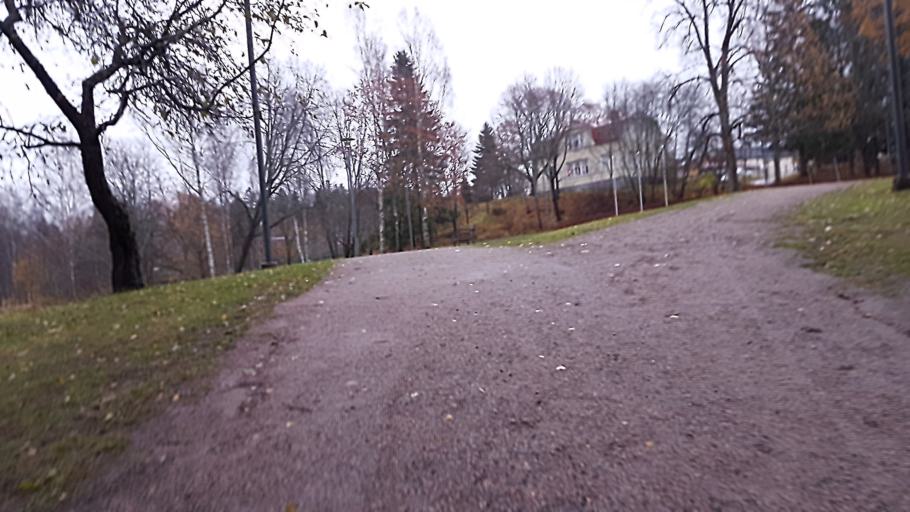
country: FI
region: Uusimaa
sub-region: Helsinki
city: Espoo
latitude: 60.2084
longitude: 24.6521
